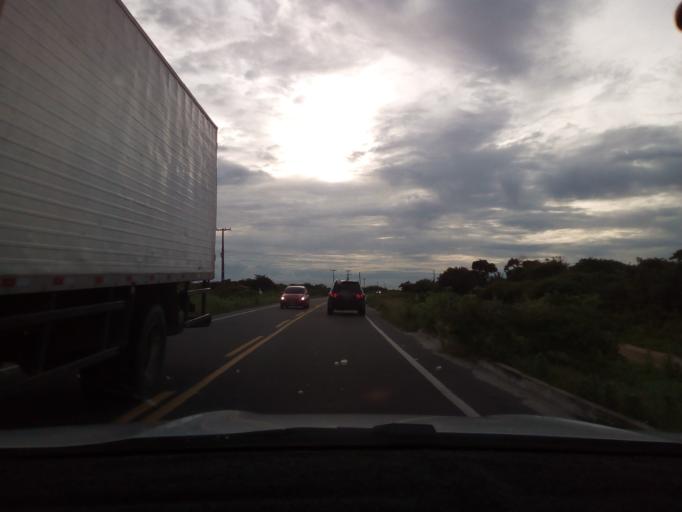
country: BR
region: Ceara
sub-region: Aracati
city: Aracati
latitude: -4.3943
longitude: -37.8662
